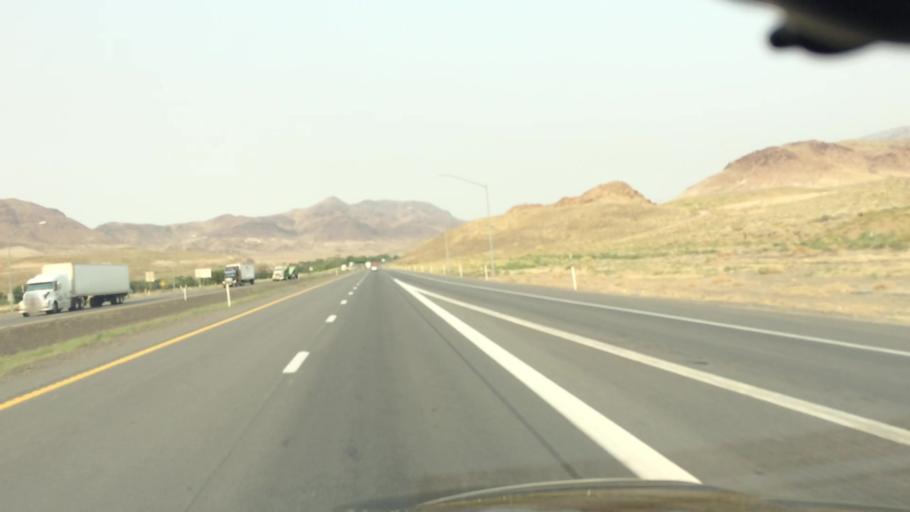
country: US
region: Nevada
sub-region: Lyon County
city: Fernley
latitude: 39.6018
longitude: -119.3384
